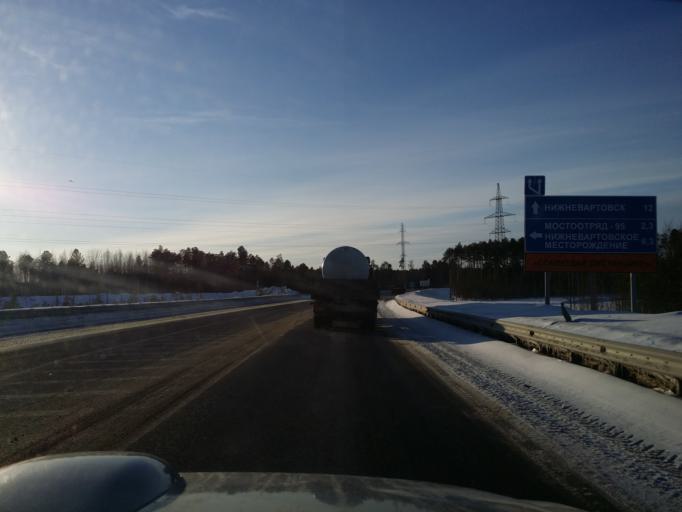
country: RU
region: Khanty-Mansiyskiy Avtonomnyy Okrug
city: Izluchinsk
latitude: 60.9353
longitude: 76.8721
